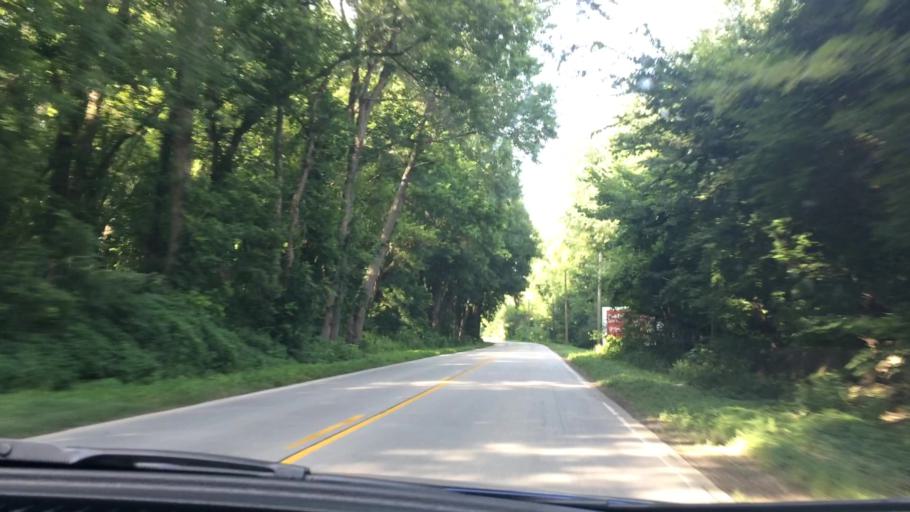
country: US
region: Indiana
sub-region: Tippecanoe County
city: West Lafayette
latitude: 40.4645
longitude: -86.8886
